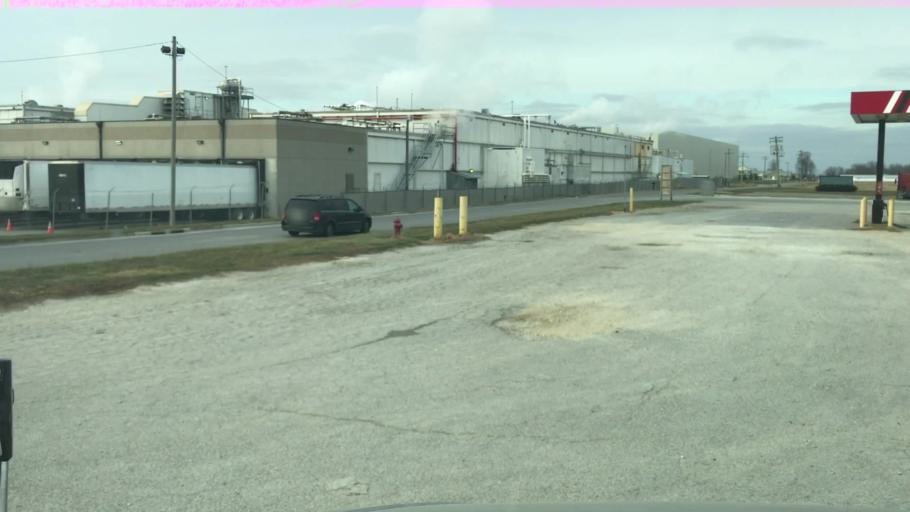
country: US
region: Illinois
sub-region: Warren County
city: Monmouth
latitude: 40.9266
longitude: -90.6402
